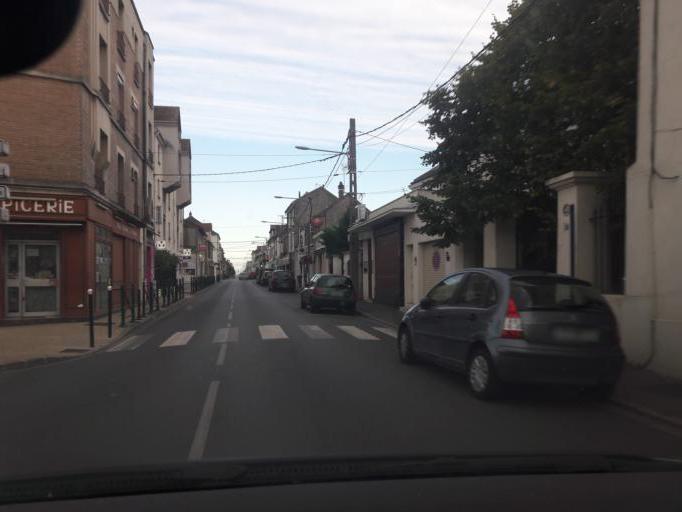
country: FR
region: Ile-de-France
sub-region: Departement de l'Essonne
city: Villemoisson-sur-Orge
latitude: 48.6730
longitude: 2.3276
